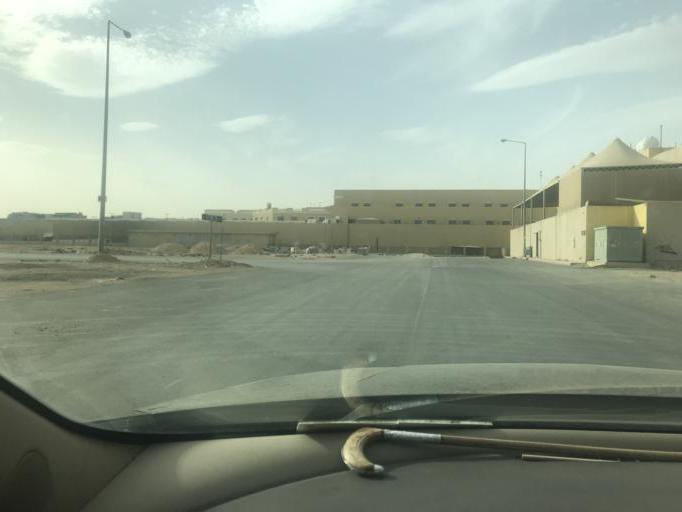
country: SA
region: Ar Riyad
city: Riyadh
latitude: 24.8065
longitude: 46.6707
